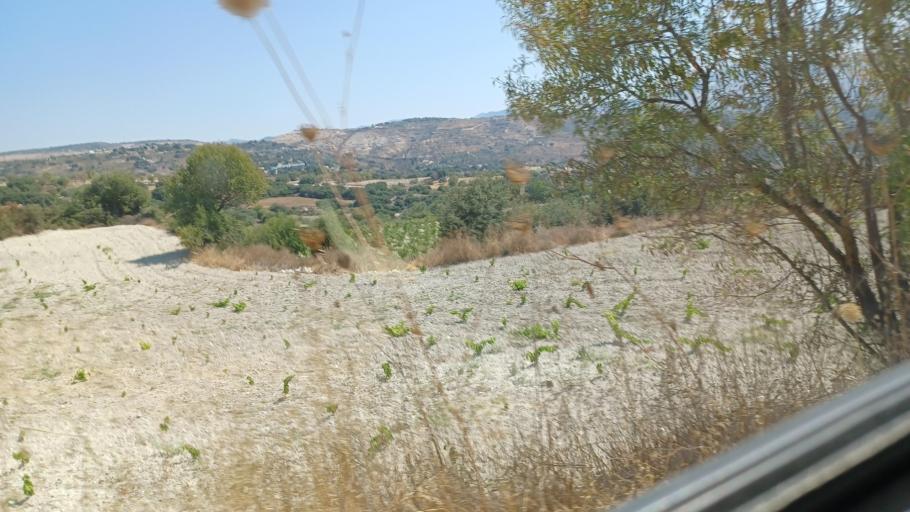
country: CY
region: Pafos
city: Mesogi
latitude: 34.8844
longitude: 32.5194
